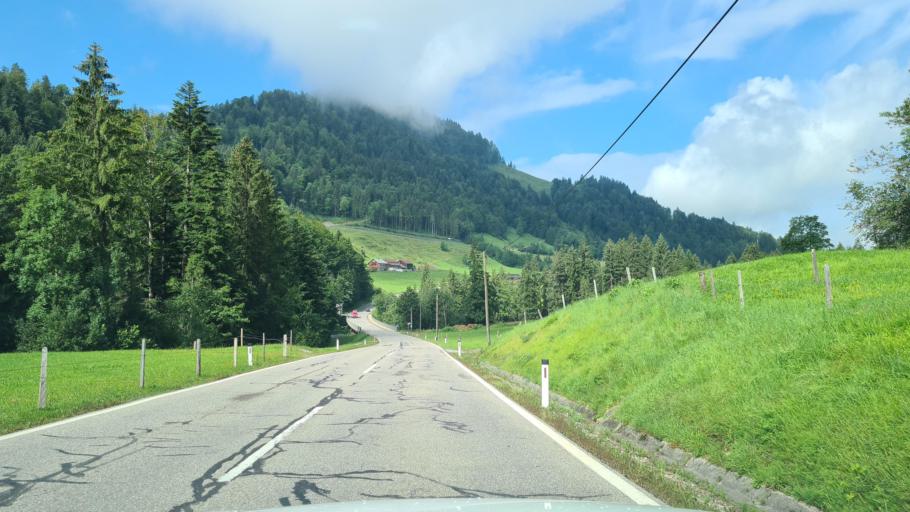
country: AT
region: Vorarlberg
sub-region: Politischer Bezirk Bregenz
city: Sibratsgfall
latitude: 47.4480
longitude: 10.0130
